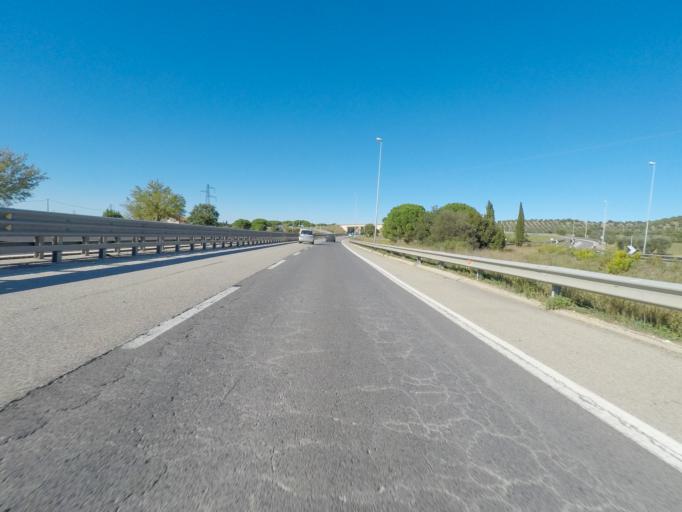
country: IT
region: Tuscany
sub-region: Provincia di Grosseto
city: Grosseto
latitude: 42.7287
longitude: 11.1362
